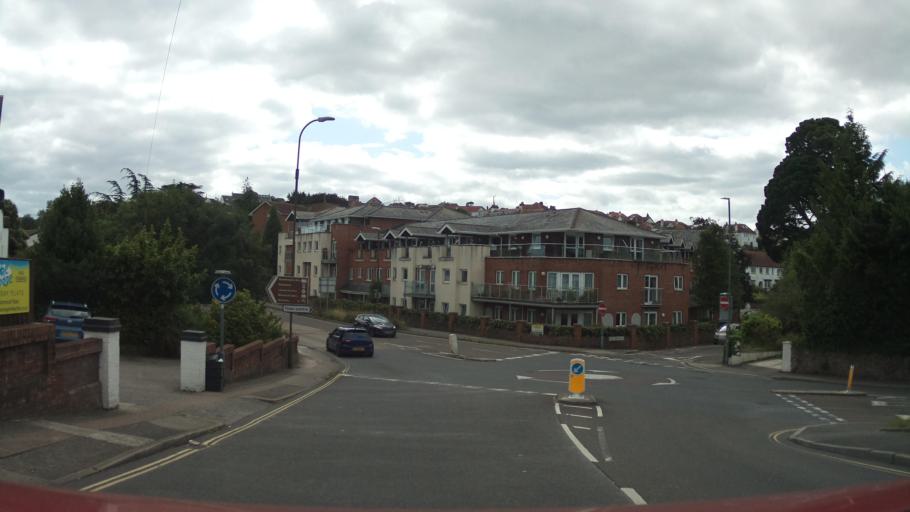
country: GB
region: England
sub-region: Borough of Torbay
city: Paignton
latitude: 50.4306
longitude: -3.5653
